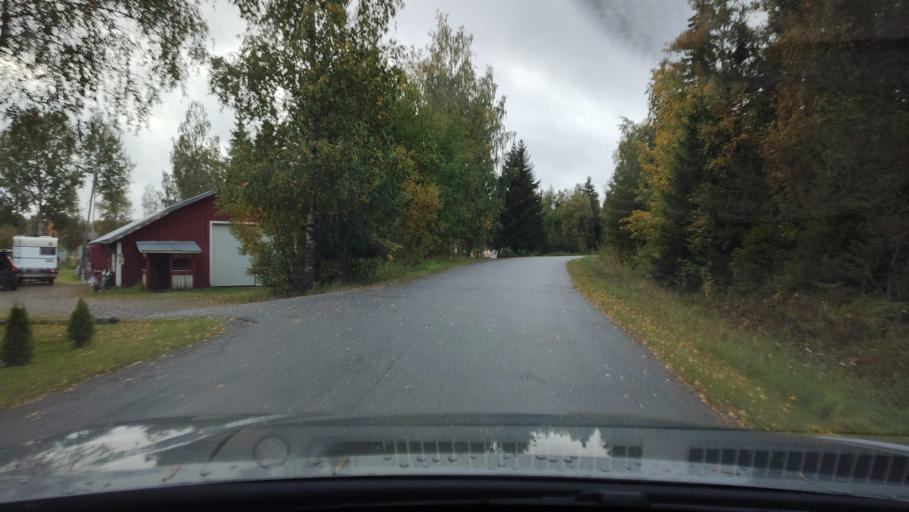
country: FI
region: Ostrobothnia
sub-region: Sydosterbotten
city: Kristinestad
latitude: 62.2641
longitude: 21.4649
